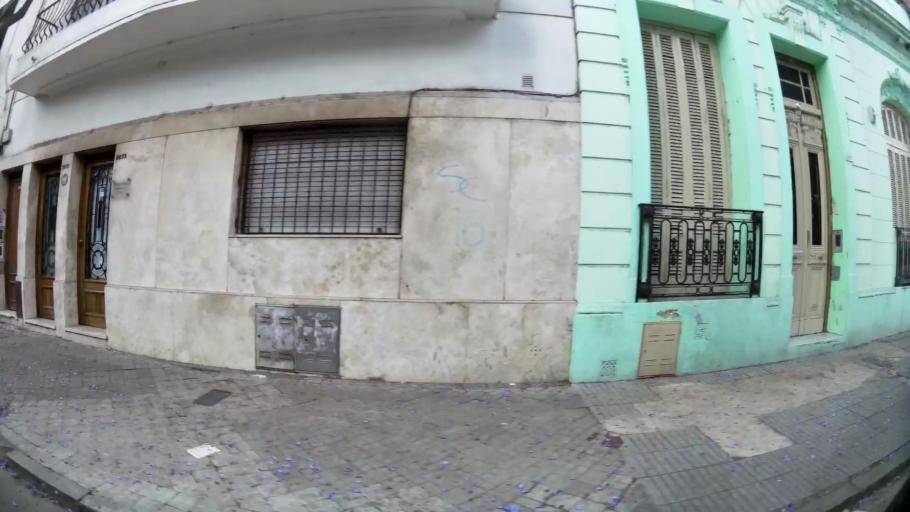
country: AR
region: Santa Fe
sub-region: Departamento de Rosario
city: Rosario
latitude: -32.9504
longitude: -60.6533
